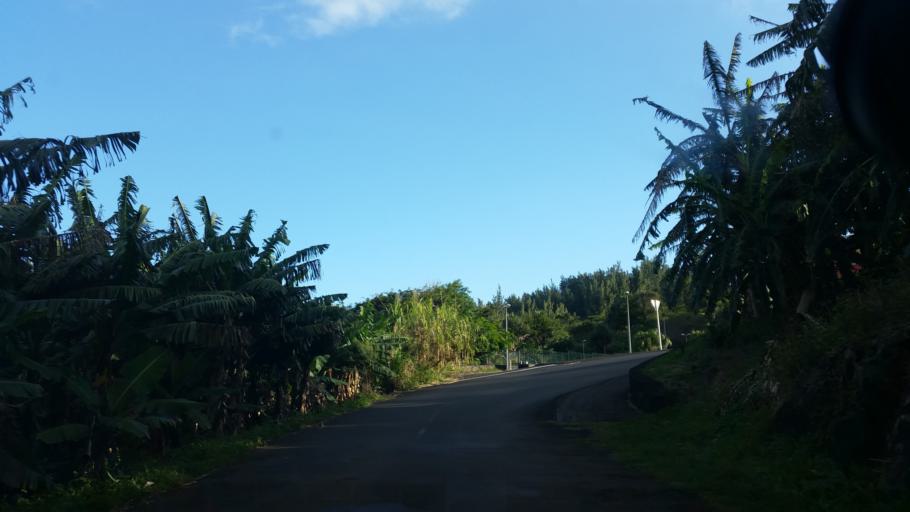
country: RE
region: Reunion
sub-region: Reunion
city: Saint-Joseph
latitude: -21.3765
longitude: 55.6690
